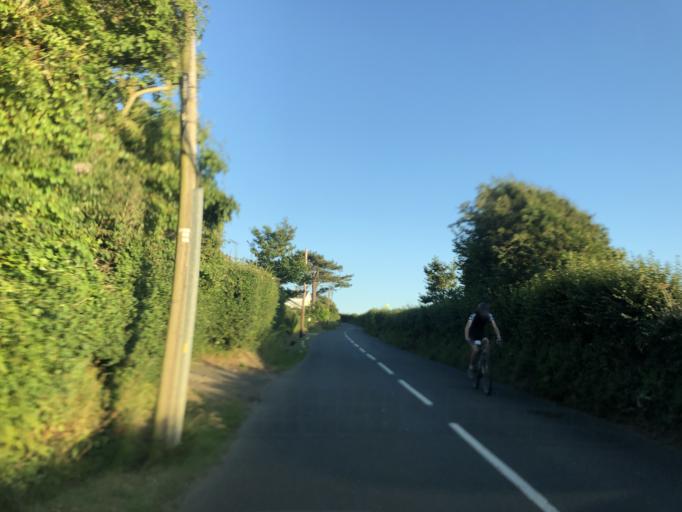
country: GB
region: England
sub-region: Isle of Wight
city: Chale
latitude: 50.6088
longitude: -1.3193
